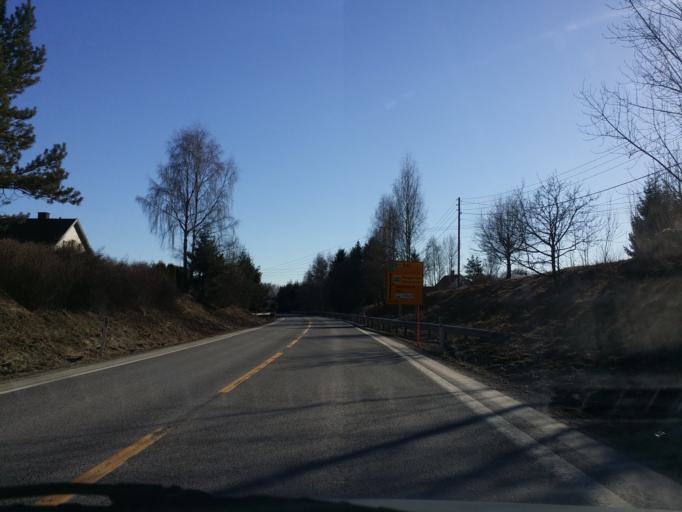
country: NO
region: Buskerud
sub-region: Ringerike
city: Honefoss
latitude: 60.2086
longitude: 10.2565
